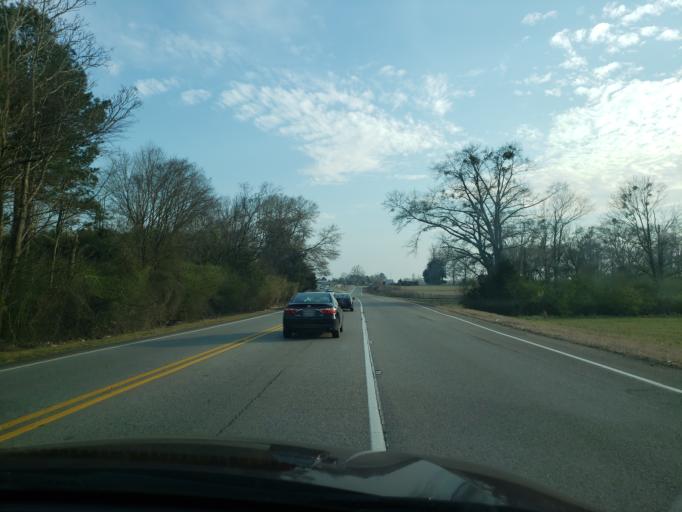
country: US
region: Alabama
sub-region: Hale County
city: Moundville
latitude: 32.9169
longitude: -87.6395
